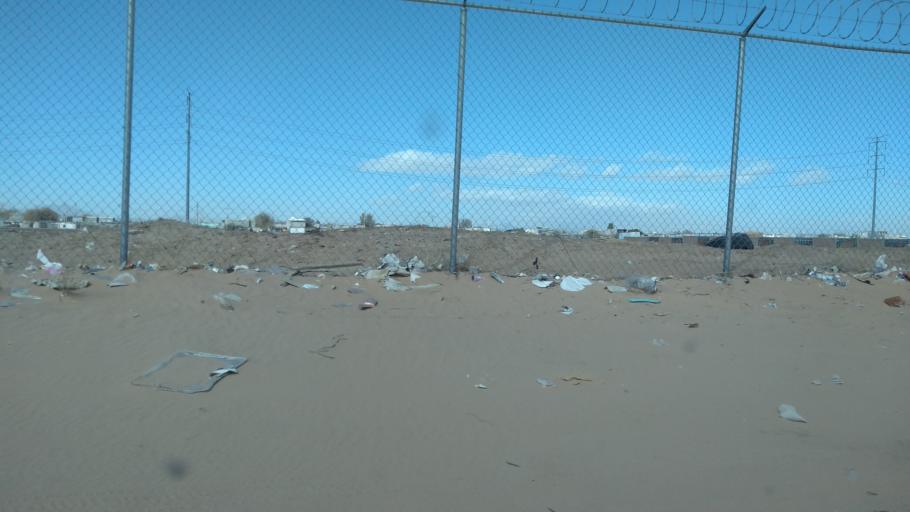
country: US
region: Texas
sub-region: El Paso County
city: Socorro Mission Number 1 Colonia
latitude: 31.5856
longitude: -106.3607
